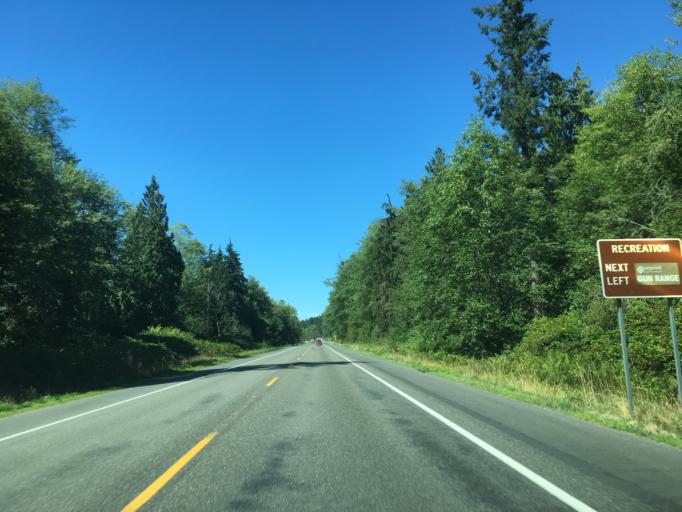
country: US
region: Washington
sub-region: Snohomish County
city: Sisco Heights
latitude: 48.1451
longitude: -122.1131
